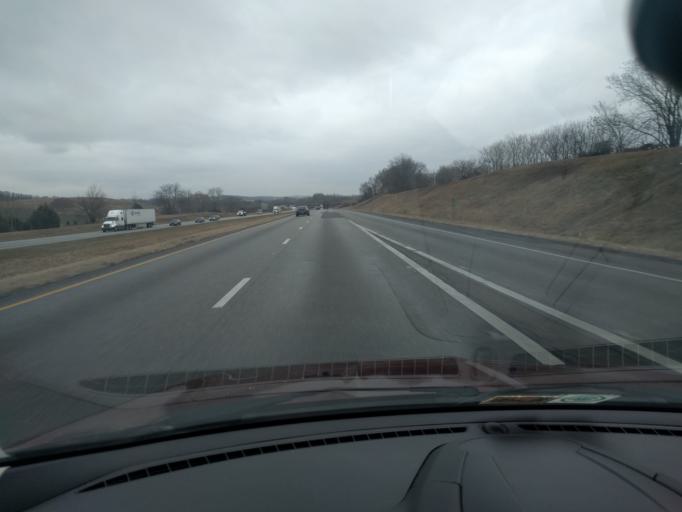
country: US
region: Virginia
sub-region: Rockingham County
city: Bridgewater
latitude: 38.3544
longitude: -78.9292
